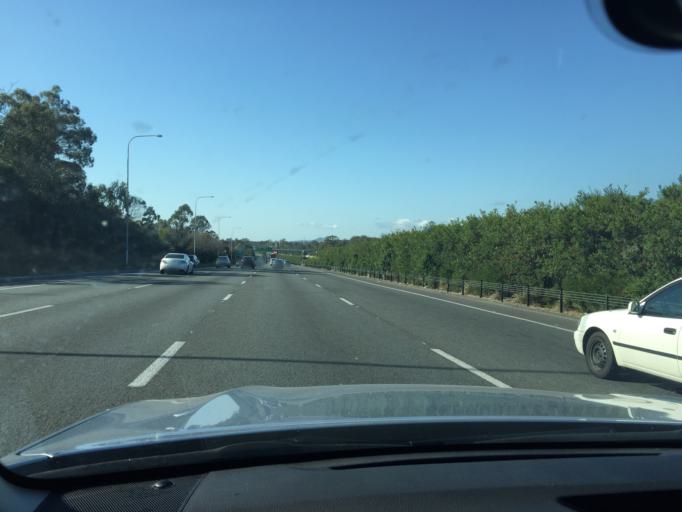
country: AU
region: Queensland
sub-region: Logan
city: Beenleigh
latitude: -27.7103
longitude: 153.2065
